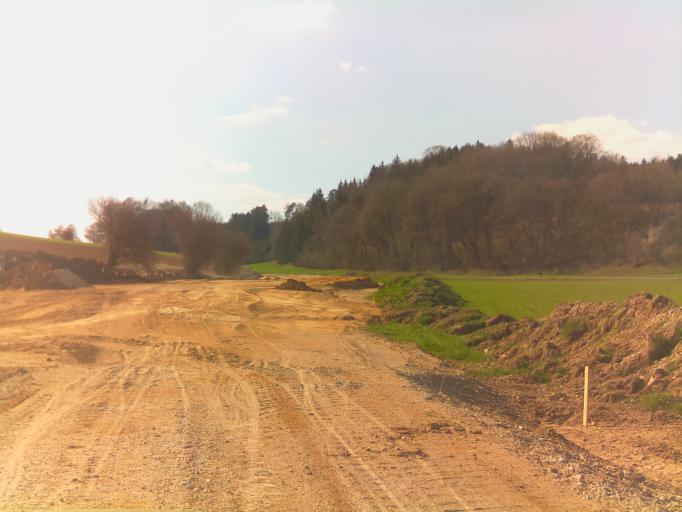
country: DE
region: Bavaria
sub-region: Swabia
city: Pottmes
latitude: 48.5845
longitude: 11.0696
